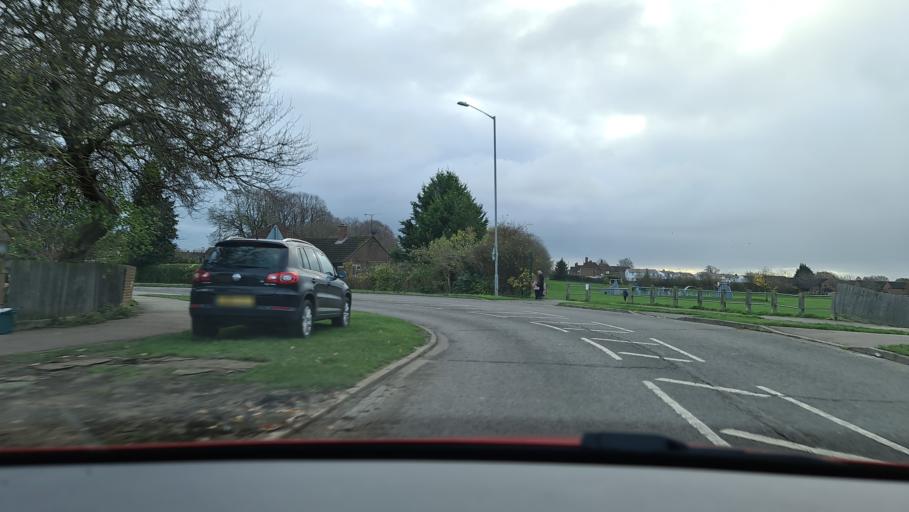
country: GB
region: England
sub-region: Buckinghamshire
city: Aylesbury
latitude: 51.8081
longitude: -0.8221
